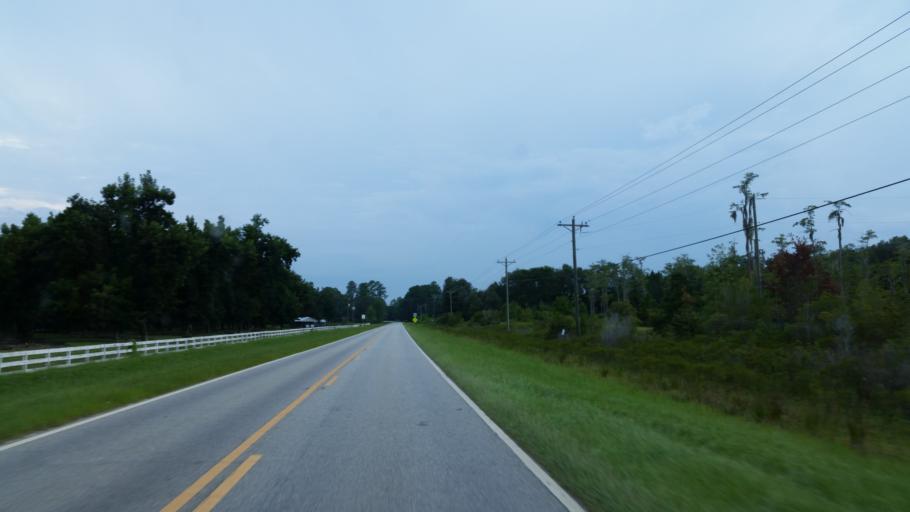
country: US
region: Georgia
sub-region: Lowndes County
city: Valdosta
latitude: 30.7401
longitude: -83.3135
